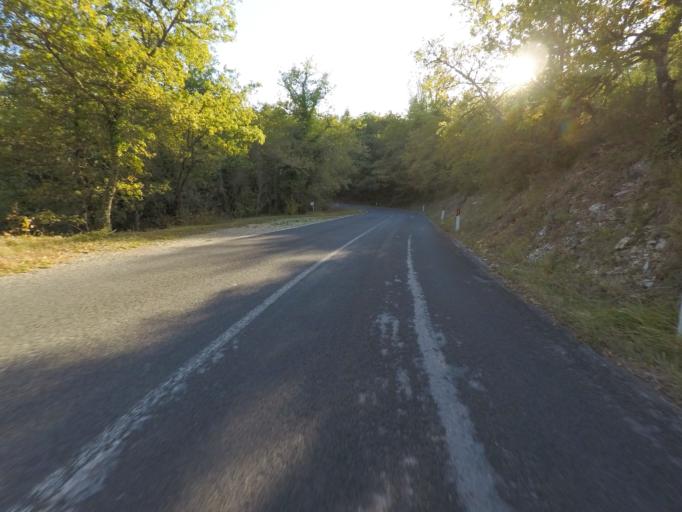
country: IT
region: Tuscany
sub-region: Provincia di Siena
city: Radda in Chianti
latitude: 43.4622
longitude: 11.3848
